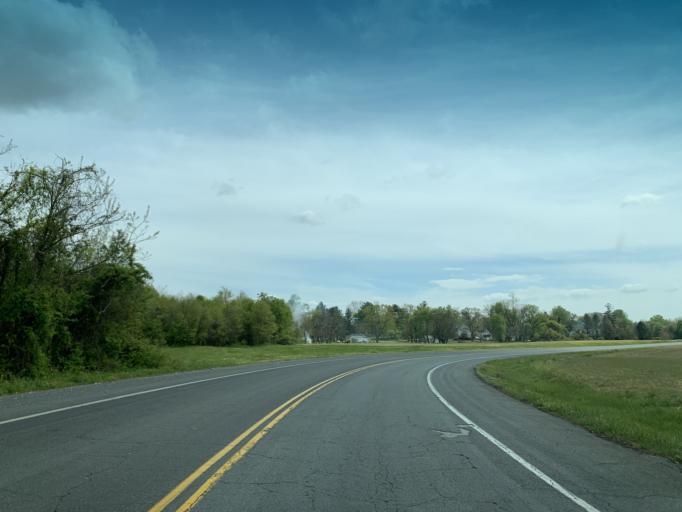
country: US
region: Maryland
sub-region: Harford County
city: Perryman
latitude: 39.4704
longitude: -76.2020
